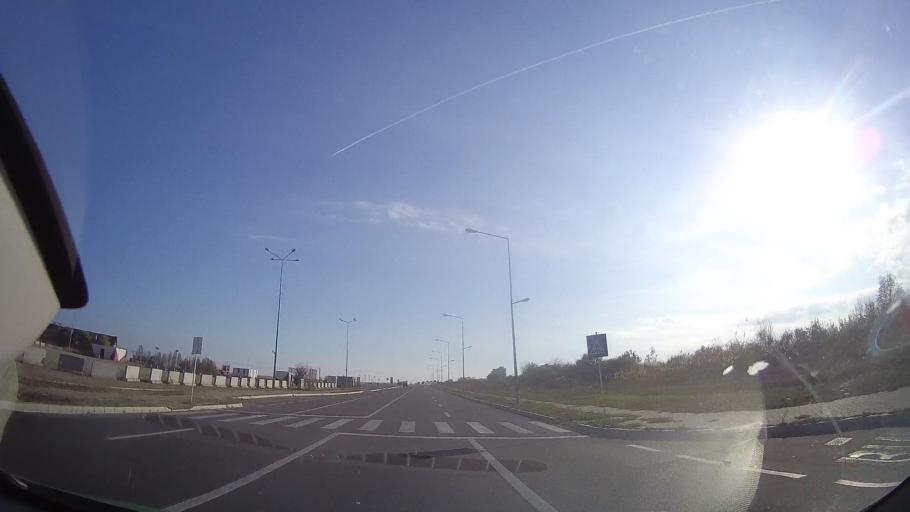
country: RO
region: Constanta
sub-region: Municipiul Mangalia
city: Mangalia
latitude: 43.8434
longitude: 28.5892
